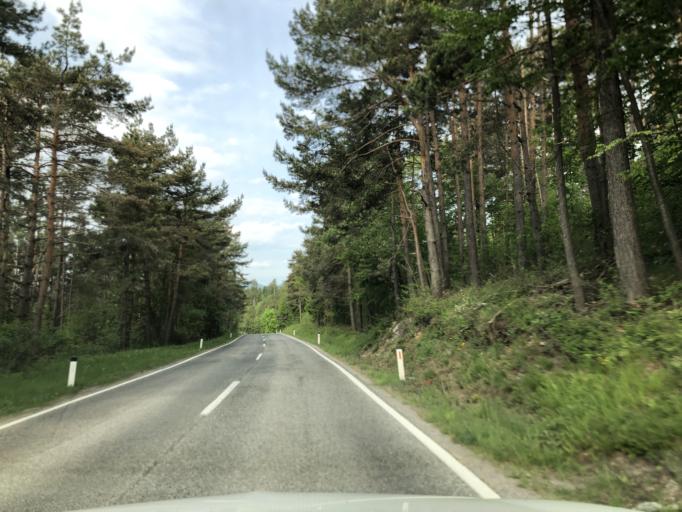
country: SI
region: Bloke
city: Nova Vas
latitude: 45.7641
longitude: 14.4741
